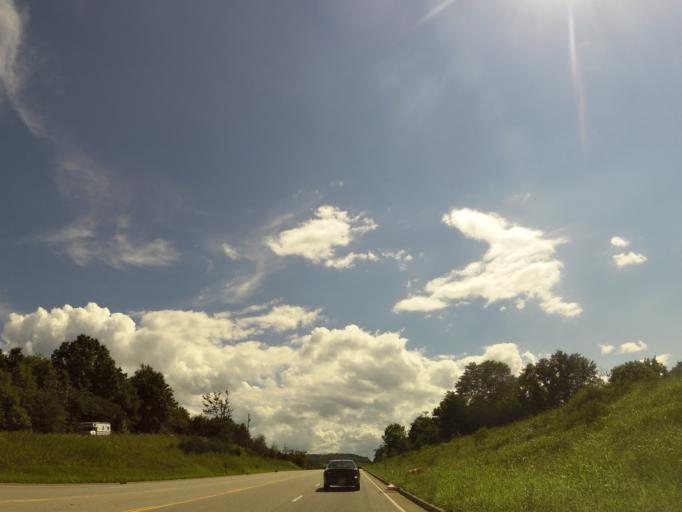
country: US
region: Tennessee
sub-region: Claiborne County
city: Tazewell
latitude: 36.4526
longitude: -83.5648
